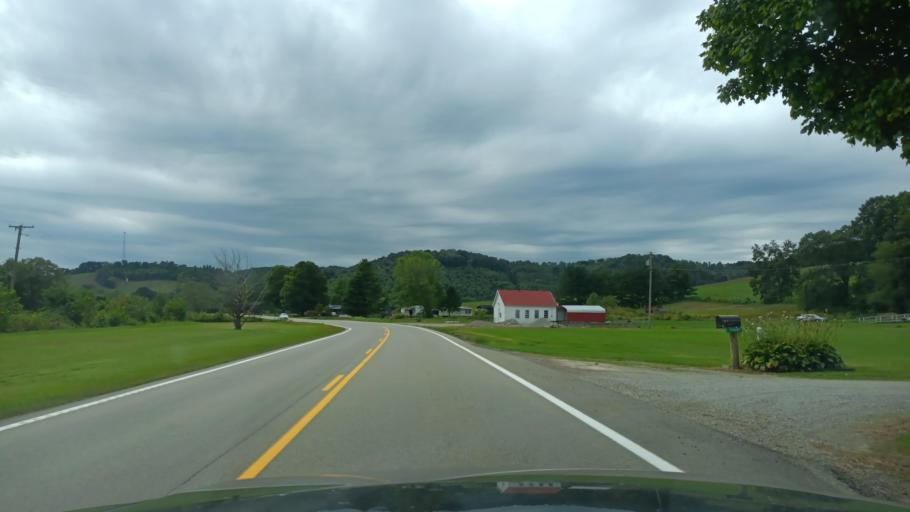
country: US
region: Ohio
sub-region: Vinton County
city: McArthur
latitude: 39.2707
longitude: -82.6710
